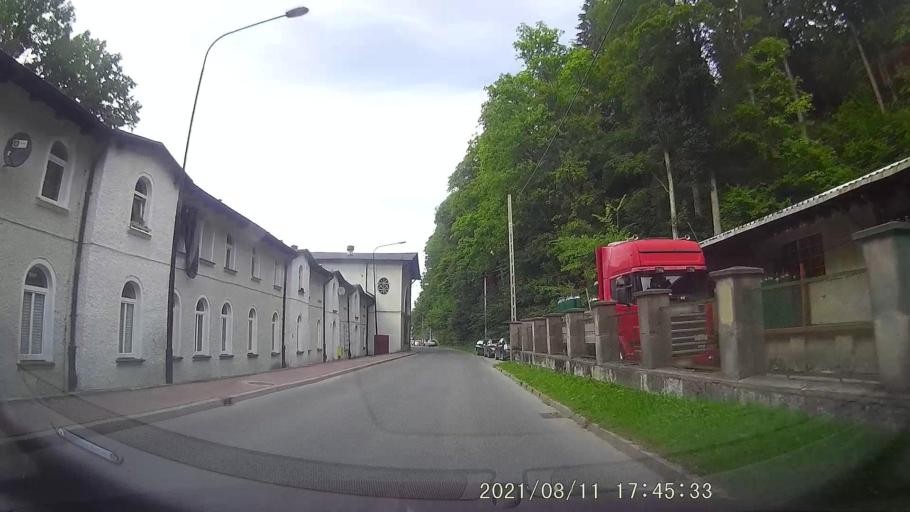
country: PL
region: Lower Silesian Voivodeship
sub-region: Powiat klodzki
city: Duszniki-Zdroj
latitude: 50.3921
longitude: 16.3831
